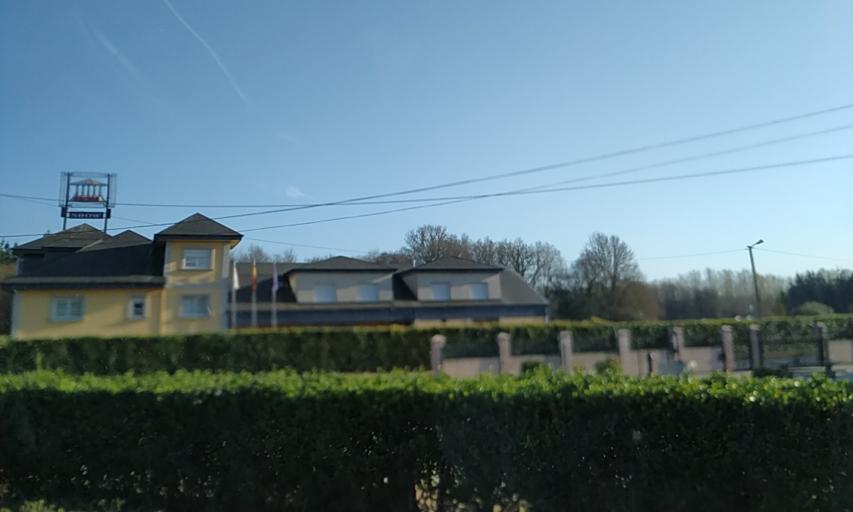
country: ES
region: Galicia
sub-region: Provincia de Lugo
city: Corgo
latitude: 42.9522
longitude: -7.4602
